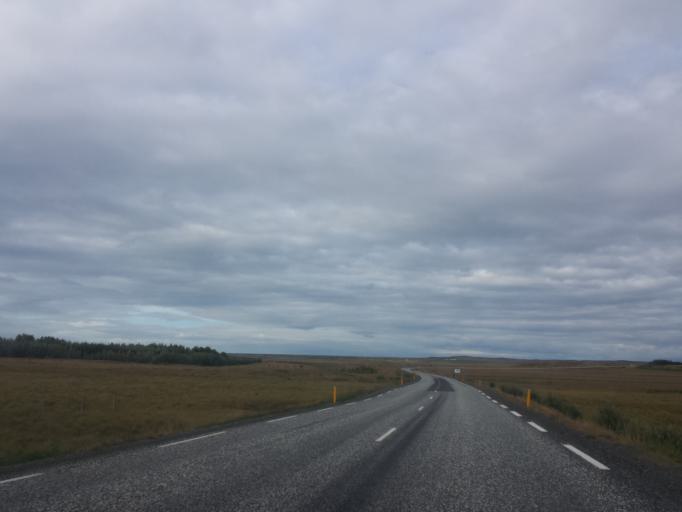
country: IS
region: West
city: Borgarnes
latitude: 64.3725
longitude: -21.8383
